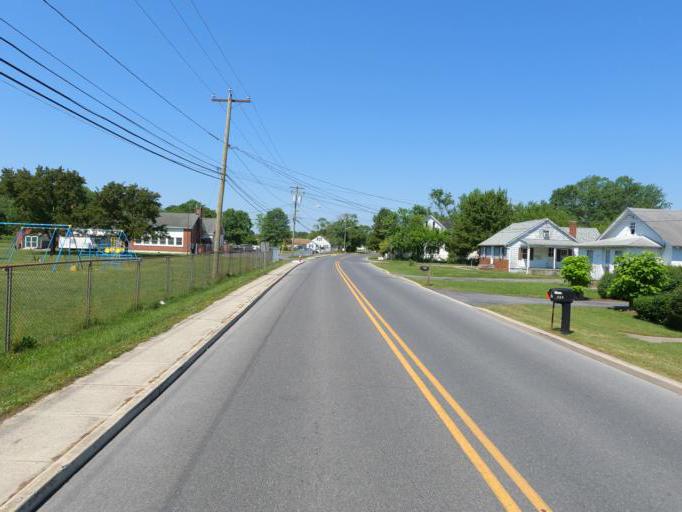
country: US
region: Delaware
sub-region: Sussex County
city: Georgetown
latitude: 38.6905
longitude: -75.3749
